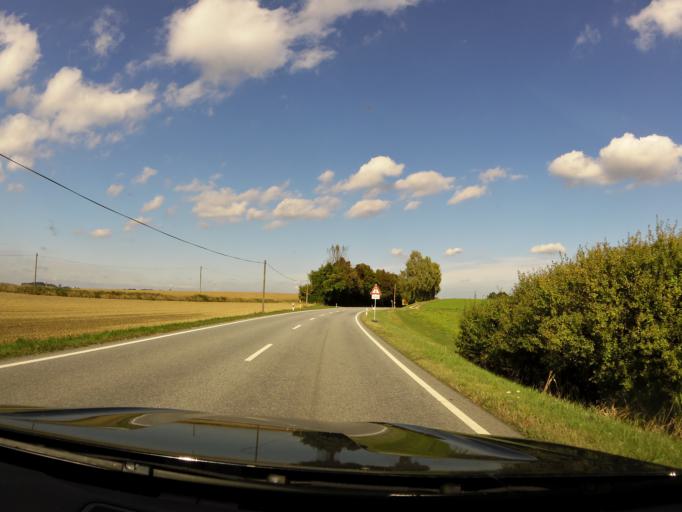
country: DE
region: Bavaria
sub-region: Lower Bavaria
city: Altfraunhofen
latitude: 48.4420
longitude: 12.1425
